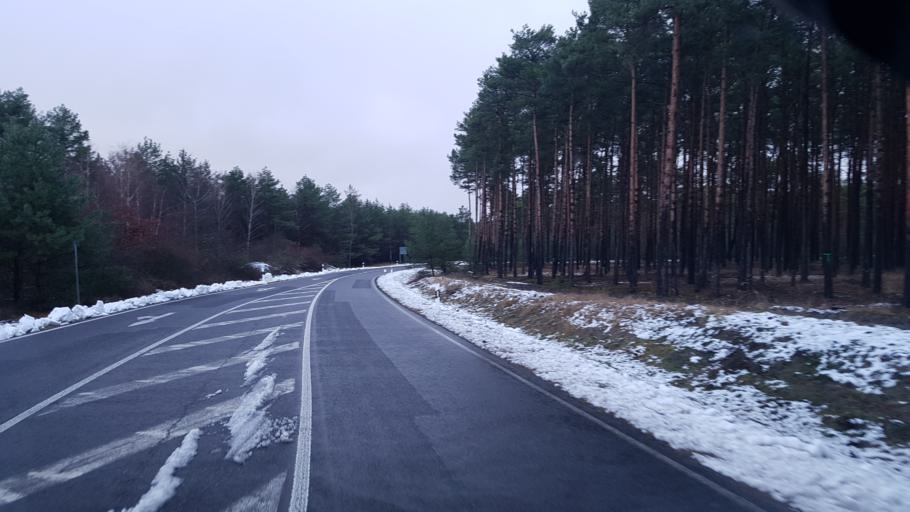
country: DE
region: Brandenburg
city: Janschwalde
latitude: 51.8488
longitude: 14.5079
